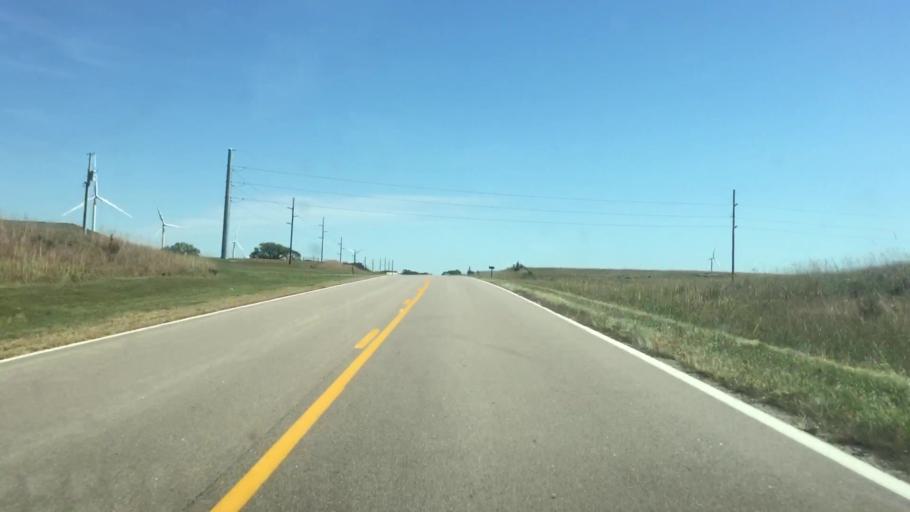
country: US
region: Nebraska
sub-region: Jefferson County
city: Fairbury
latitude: 40.0448
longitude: -96.9654
